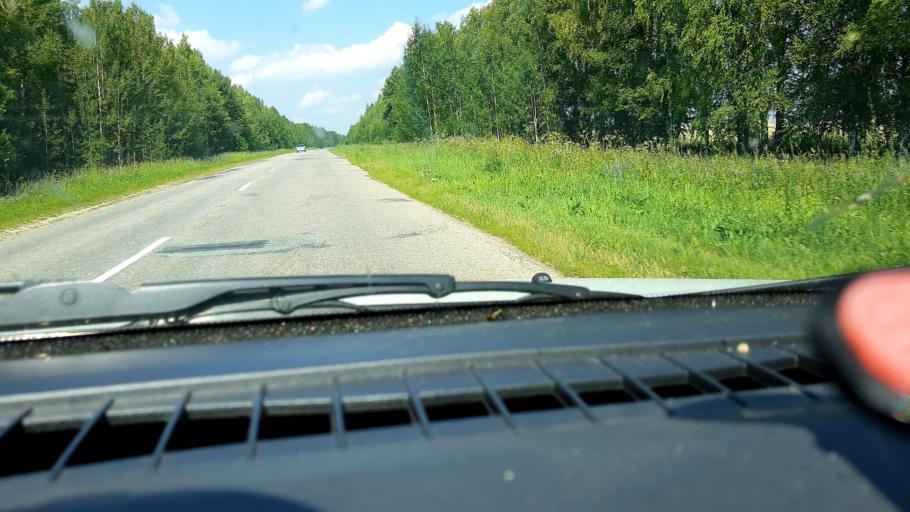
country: RU
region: Nizjnij Novgorod
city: Sharanga
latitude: 57.0620
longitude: 46.5446
